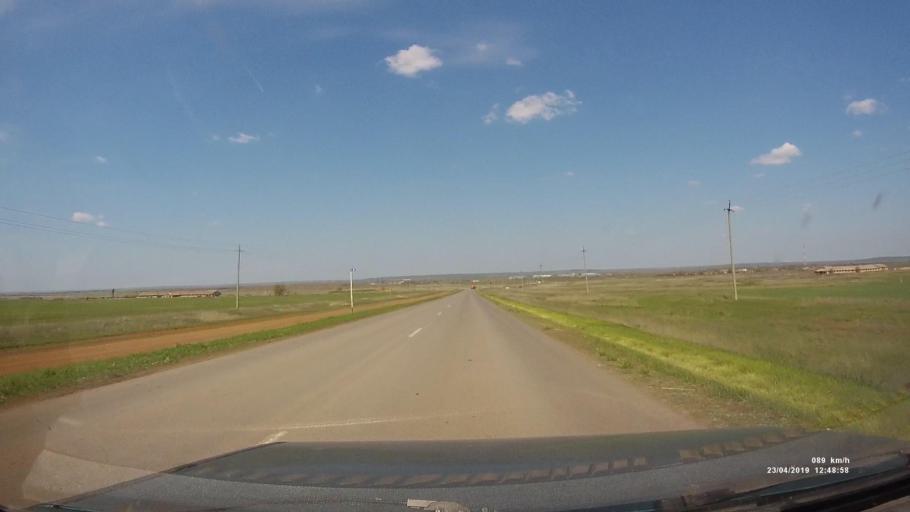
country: RU
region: Kalmykiya
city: Yashalta
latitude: 46.5314
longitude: 42.6389
